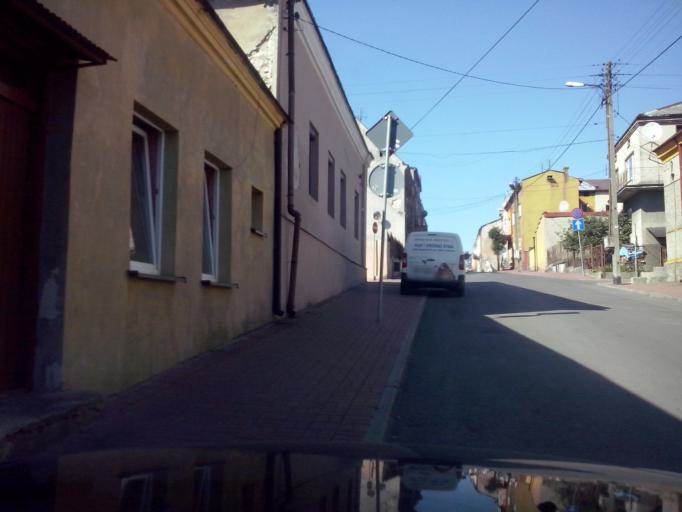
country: PL
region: Swietokrzyskie
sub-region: Powiat kielecki
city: Chmielnik
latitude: 50.6132
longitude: 20.7521
